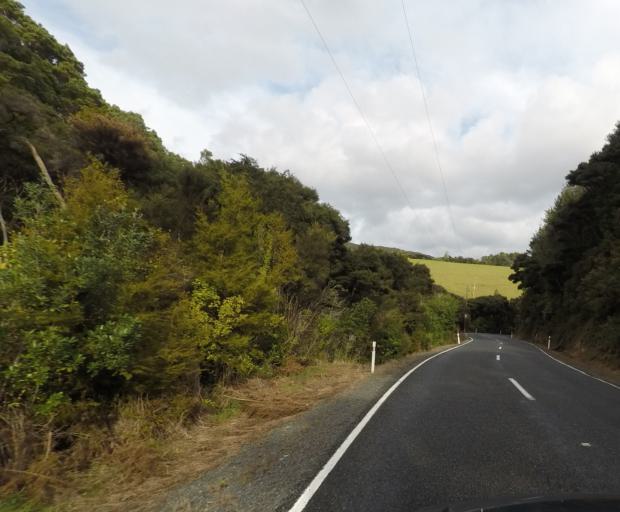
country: NZ
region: Northland
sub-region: Whangarei
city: Ruakaka
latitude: -36.0522
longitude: 174.5447
